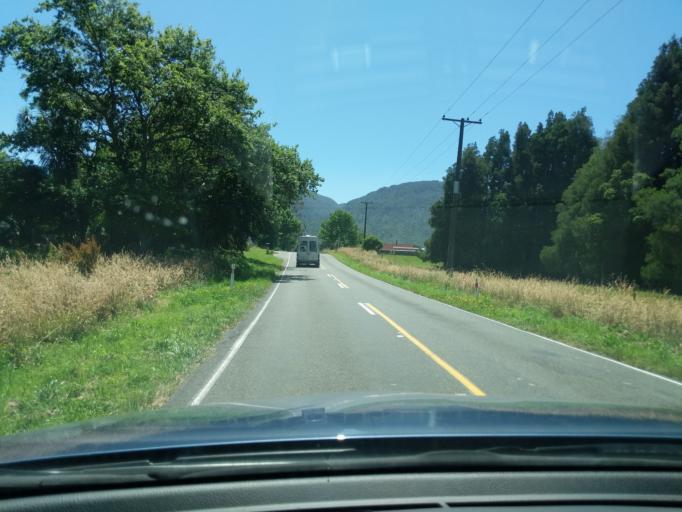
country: NZ
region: Tasman
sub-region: Tasman District
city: Takaka
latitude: -40.7040
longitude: 172.6356
